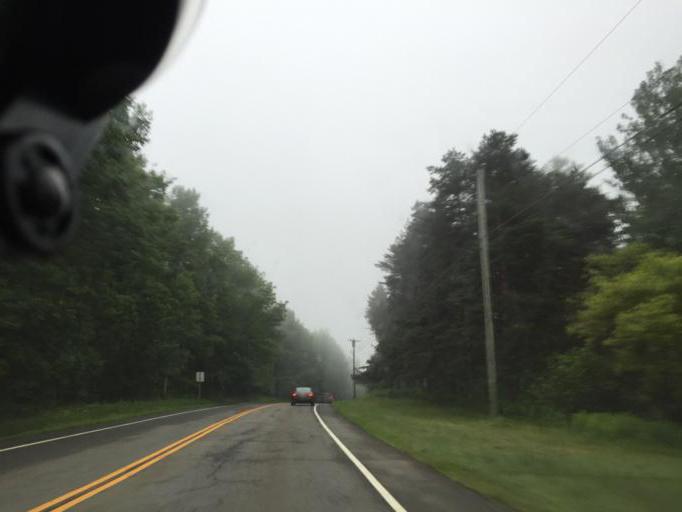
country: US
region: Connecticut
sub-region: Litchfield County
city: Winchester Center
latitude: 41.8839
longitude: -73.2536
